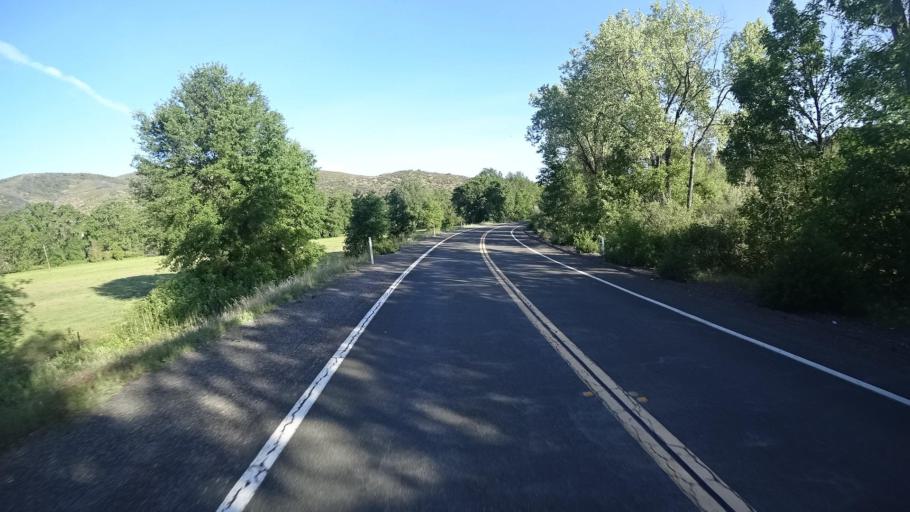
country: US
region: California
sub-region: Lake County
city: North Lakeport
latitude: 39.1069
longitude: -122.9743
